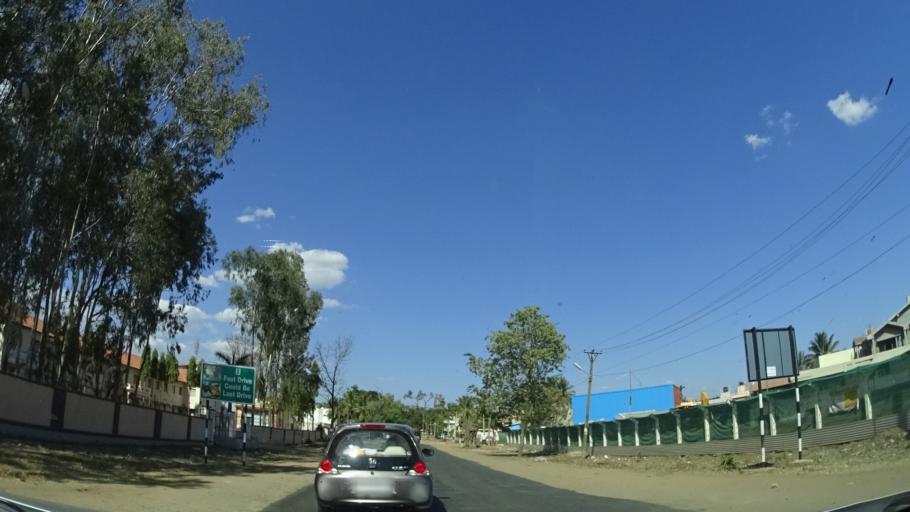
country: IN
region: Karnataka
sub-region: Chikmagalur
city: Chikmagalur
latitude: 13.3293
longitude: 75.7871
